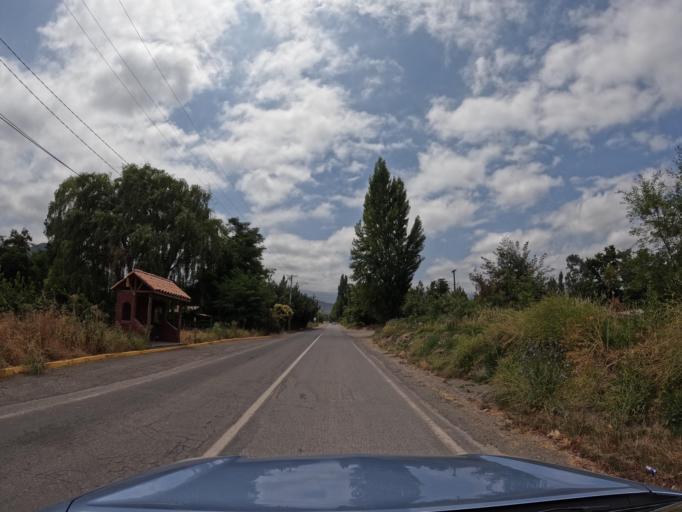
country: CL
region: O'Higgins
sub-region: Provincia de Colchagua
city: Chimbarongo
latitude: -34.7450
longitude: -70.9646
